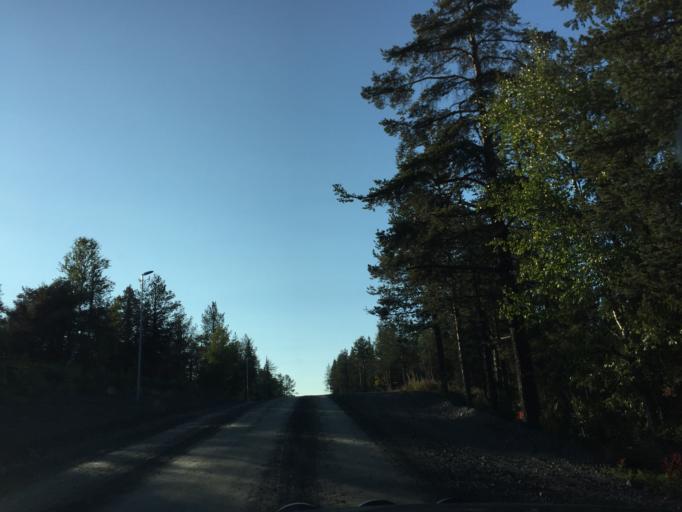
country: SE
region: Norrbotten
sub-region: Gallivare Kommun
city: Malmberget
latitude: 67.6434
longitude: 21.0294
